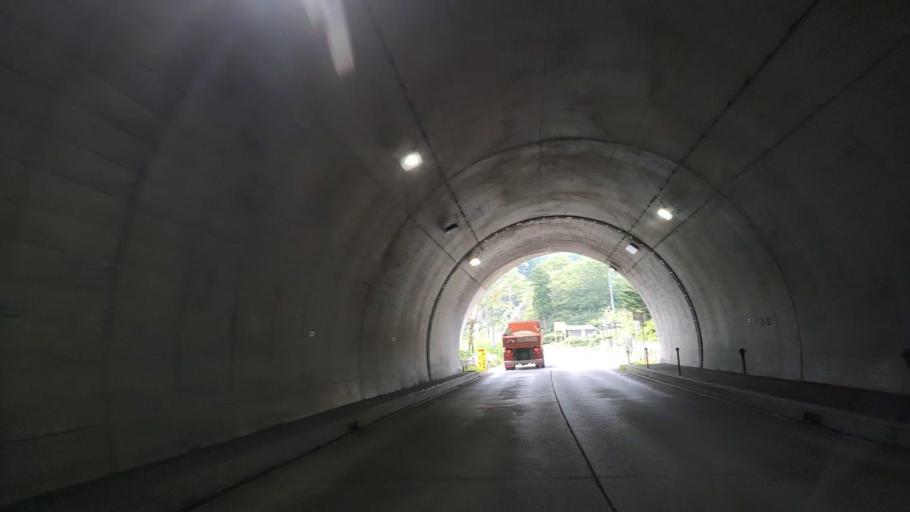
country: JP
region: Nagano
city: Iiyama
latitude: 36.9098
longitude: 138.3160
